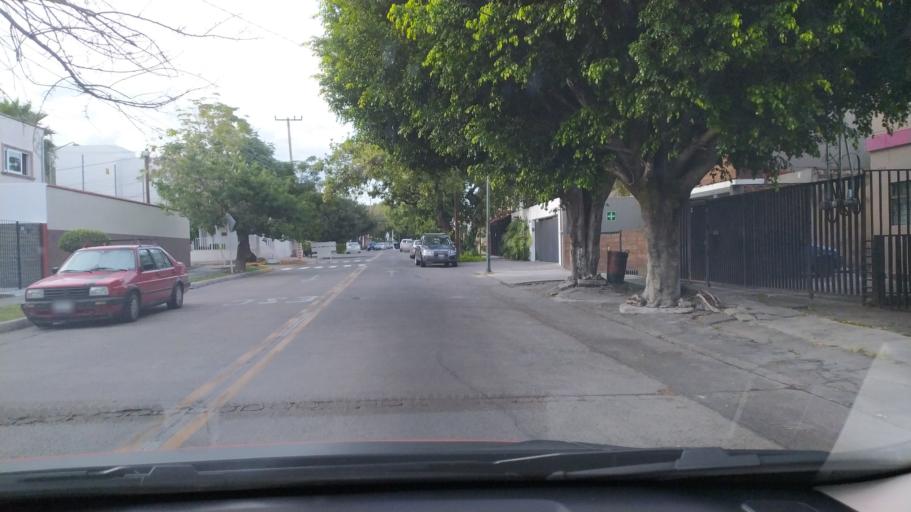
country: MX
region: Jalisco
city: Guadalajara
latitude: 20.6607
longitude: -103.4040
